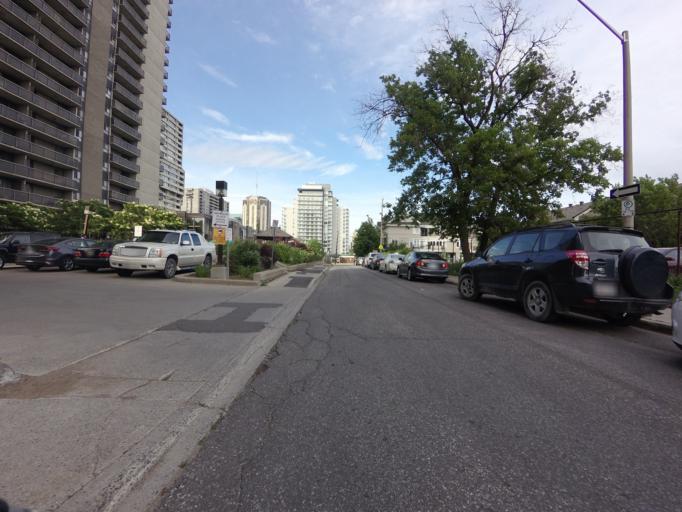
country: CA
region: Ontario
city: Ottawa
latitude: 45.4141
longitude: -75.7063
